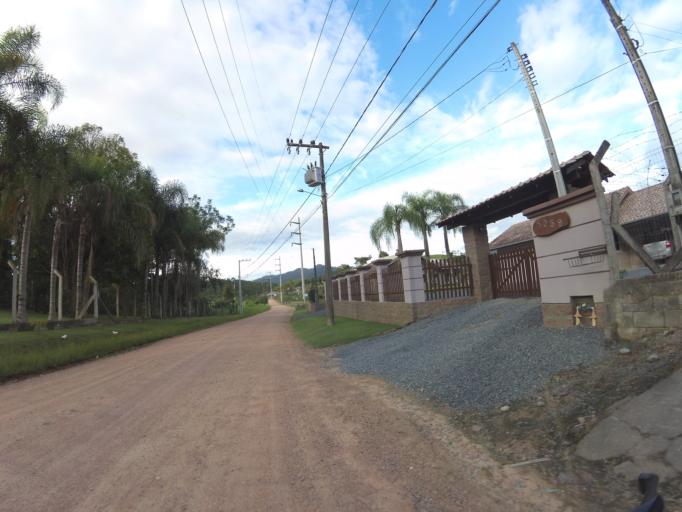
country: BR
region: Santa Catarina
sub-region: Pomerode
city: Pomerode
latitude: -26.7990
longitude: -49.1585
